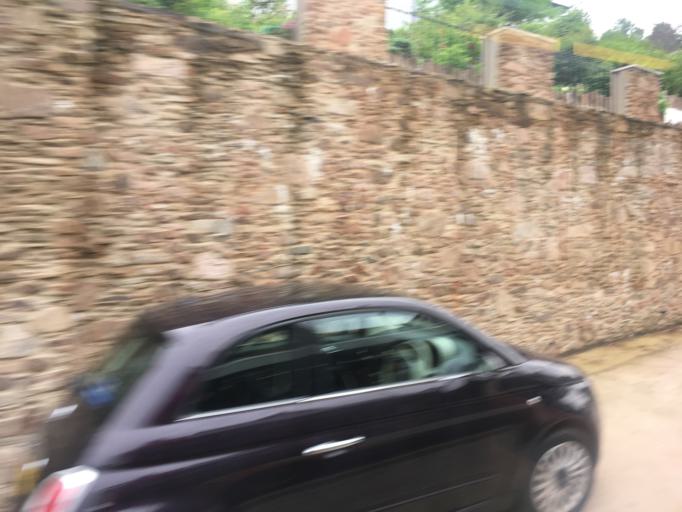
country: GB
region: England
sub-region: Devon
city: Dartmouth
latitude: 50.3502
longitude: -3.5858
